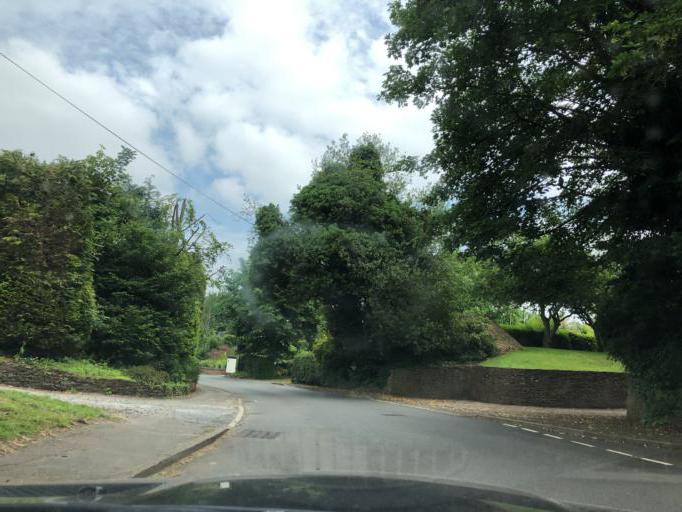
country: GB
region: England
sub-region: Warwickshire
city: Kenilworth
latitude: 52.3186
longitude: -1.5793
